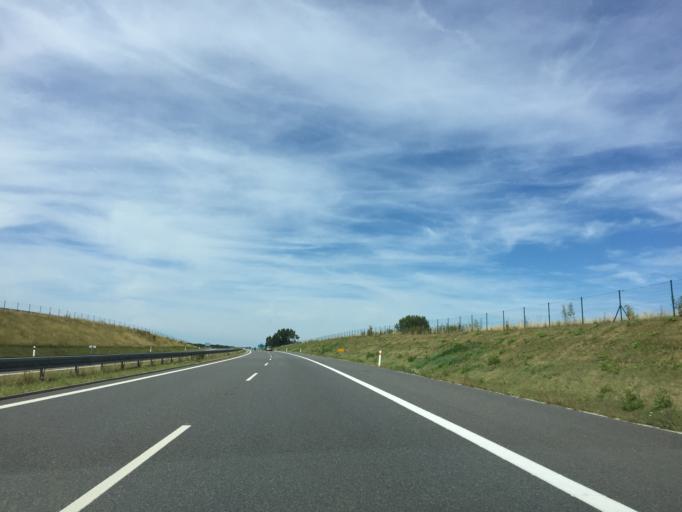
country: CZ
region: Jihocesky
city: Sobeslav
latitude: 49.2595
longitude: 14.7370
